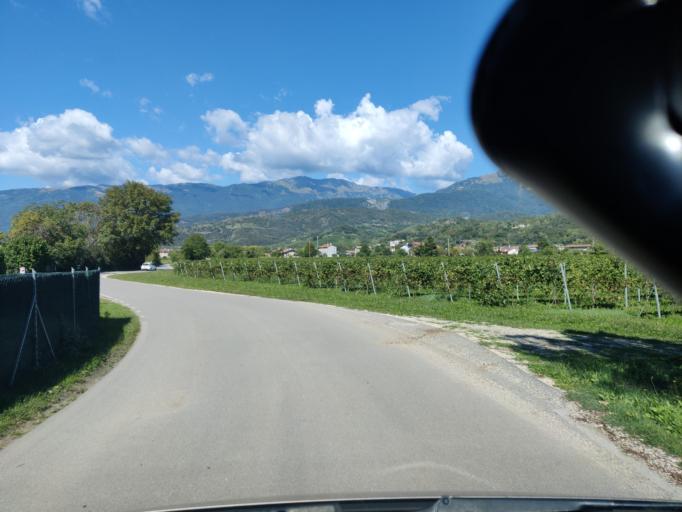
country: IT
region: Veneto
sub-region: Provincia di Treviso
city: Cappella Maggiore
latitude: 45.9734
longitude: 12.3366
